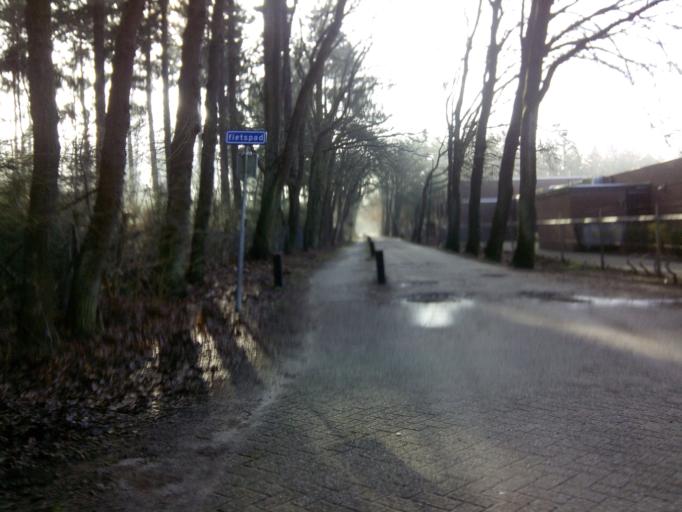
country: NL
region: Utrecht
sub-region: Gemeente Utrechtse Heuvelrug
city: Maarn
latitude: 52.0604
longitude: 5.3761
